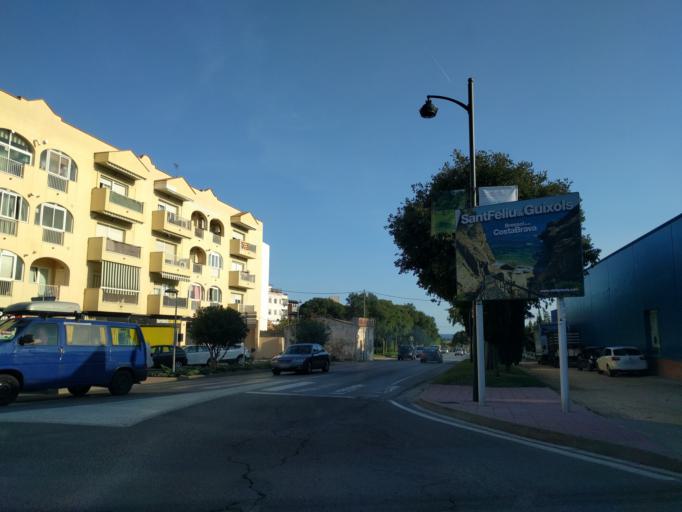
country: ES
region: Catalonia
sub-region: Provincia de Girona
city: Sant Feliu de Guixols
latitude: 41.7935
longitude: 3.0203
